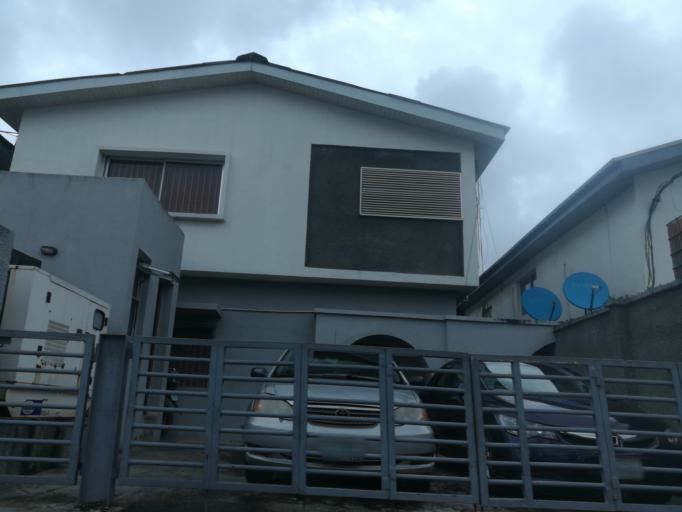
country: NG
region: Lagos
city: Ikoyi
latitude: 6.4403
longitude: 3.4181
